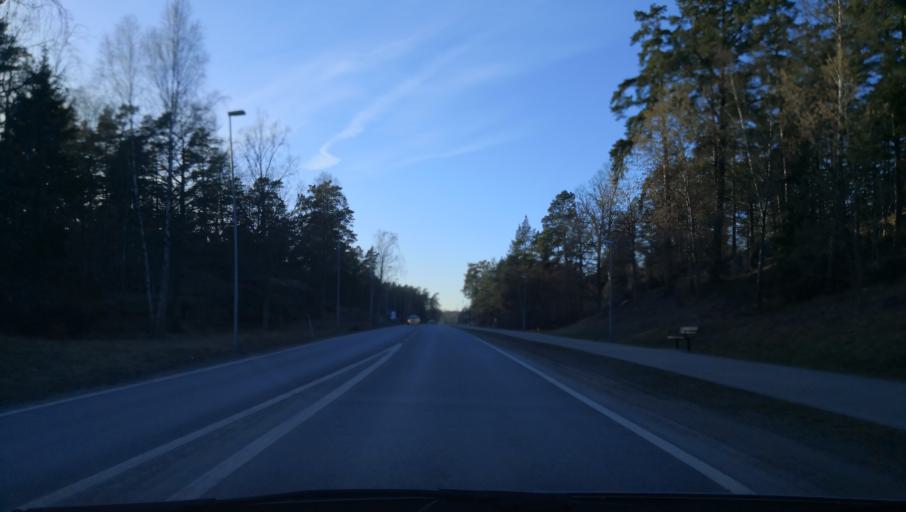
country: SE
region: Stockholm
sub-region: Varmdo Kommun
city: Gustavsberg
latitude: 59.3173
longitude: 18.4138
